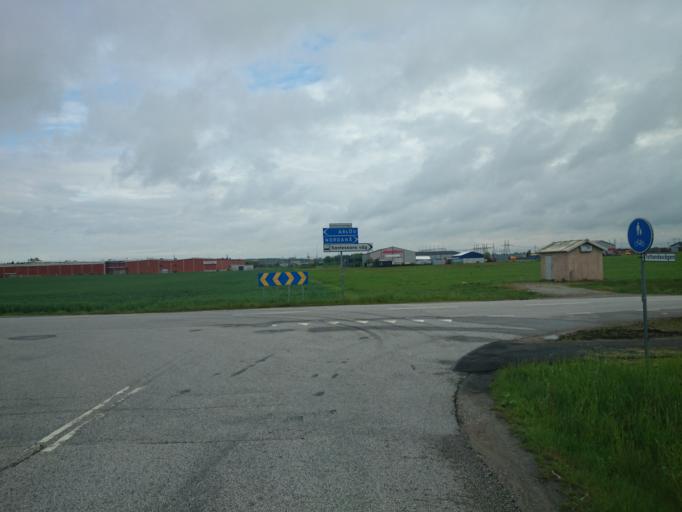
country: SE
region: Skane
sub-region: Burlovs Kommun
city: Arloev
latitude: 55.6121
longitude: 13.0914
